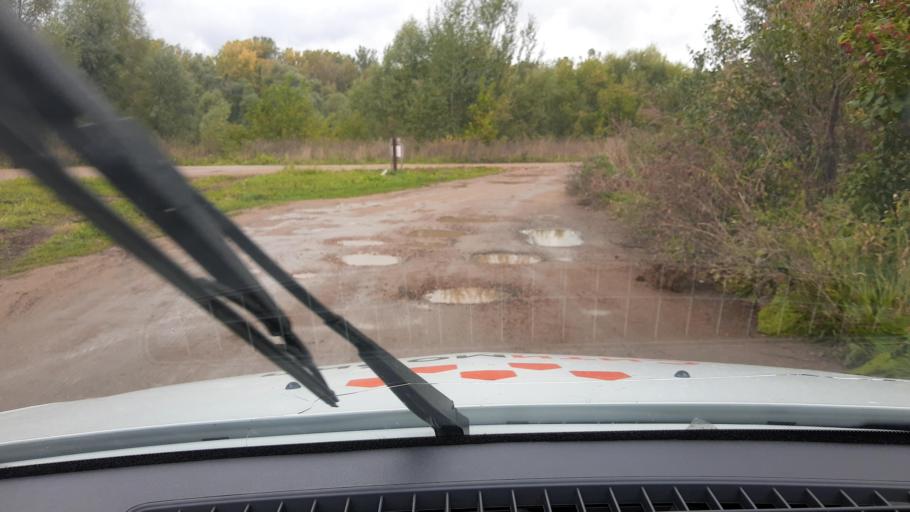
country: RU
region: Bashkortostan
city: Iglino
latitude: 54.7780
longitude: 56.2016
